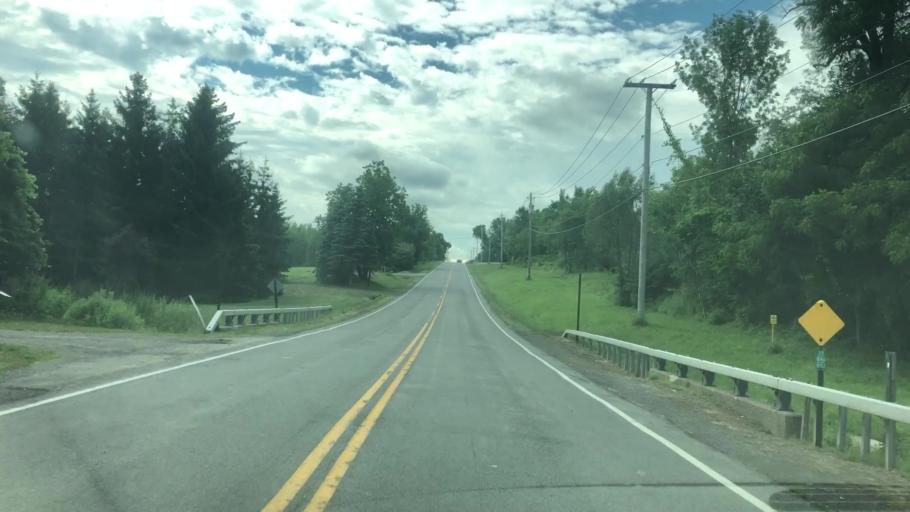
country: US
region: New York
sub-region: Monroe County
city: Fairport
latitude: 43.0722
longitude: -77.3922
